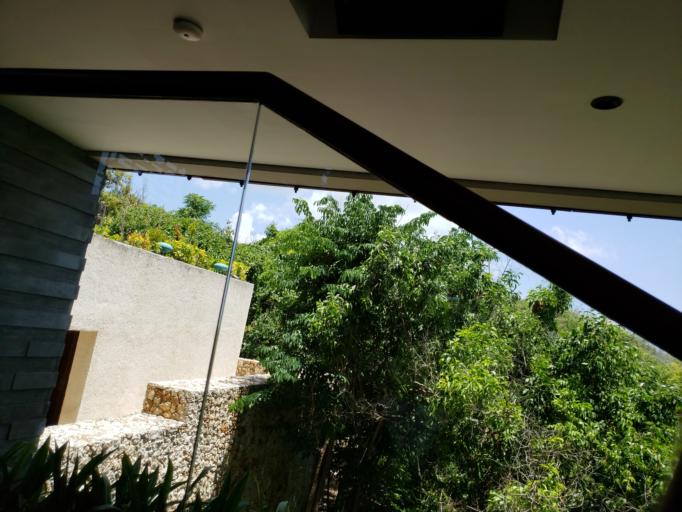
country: ID
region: Bali
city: Kangin
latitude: -8.8462
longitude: 115.1407
